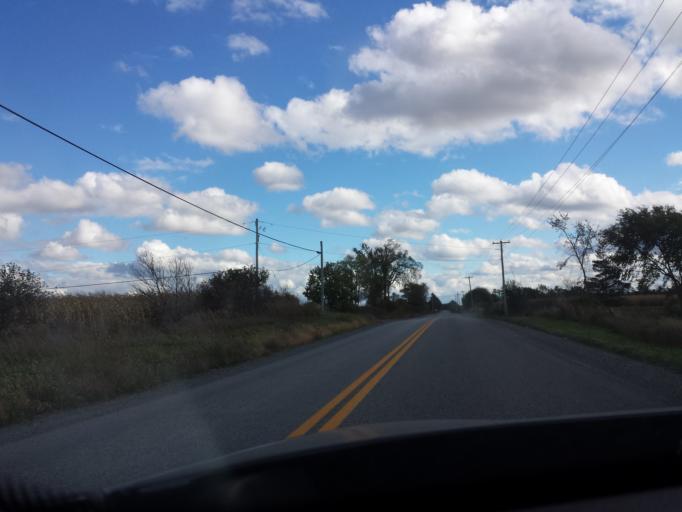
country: CA
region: Ontario
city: Carleton Place
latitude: 45.1838
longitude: -76.1129
